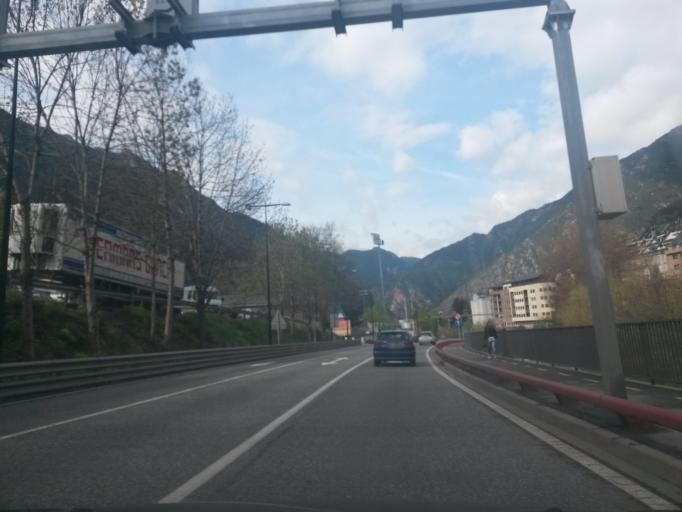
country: AD
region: Andorra la Vella
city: Andorra la Vella
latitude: 42.5031
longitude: 1.5155
